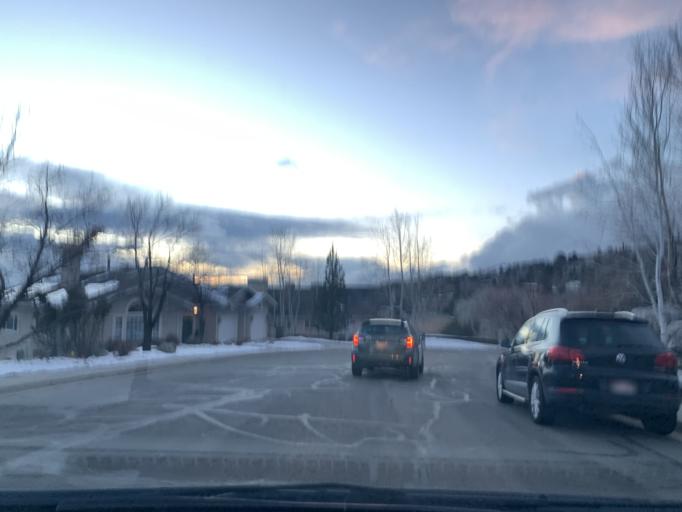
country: US
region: Utah
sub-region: Salt Lake County
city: Salt Lake City
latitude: 40.7822
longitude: -111.8602
